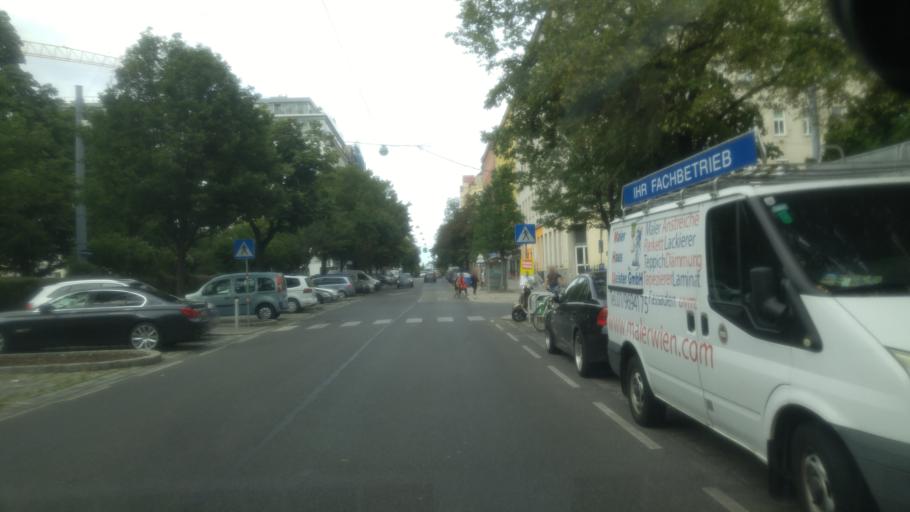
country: AT
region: Vienna
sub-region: Wien Stadt
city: Vienna
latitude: 48.2373
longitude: 16.3857
